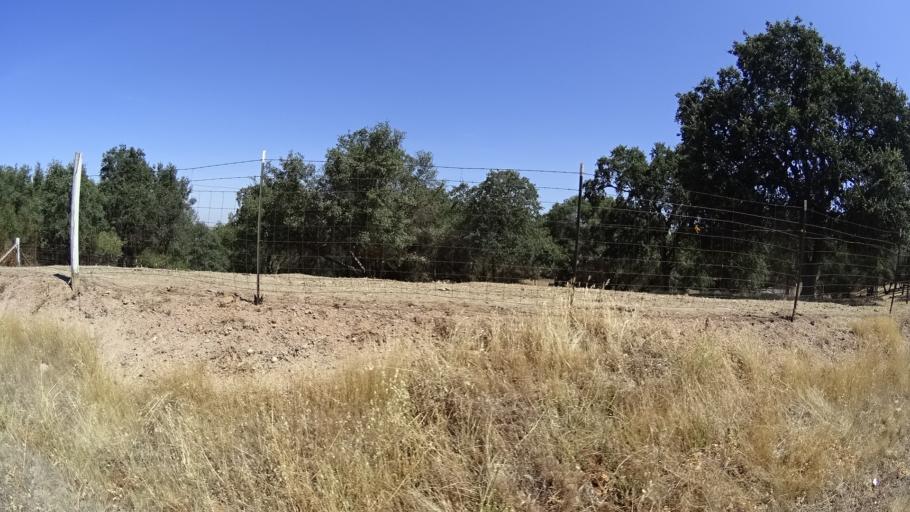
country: US
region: California
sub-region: Calaveras County
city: Rancho Calaveras
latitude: 38.1484
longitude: -120.9399
